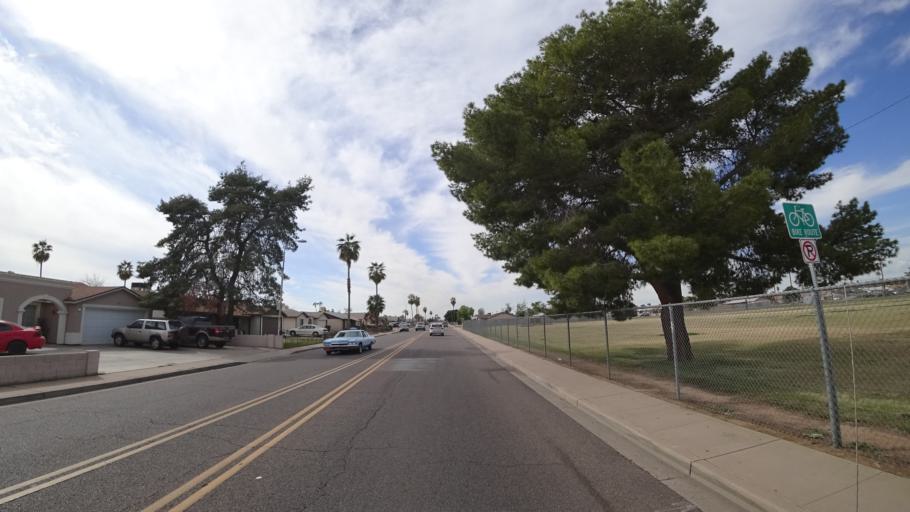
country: US
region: Arizona
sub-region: Maricopa County
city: Glendale
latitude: 33.4733
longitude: -112.1873
